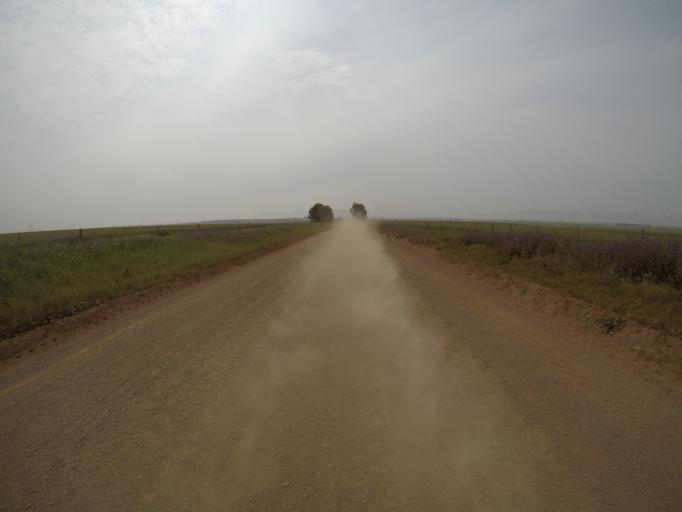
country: ZA
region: Western Cape
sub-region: City of Cape Town
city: Kraaifontein
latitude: -33.7192
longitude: 18.6782
